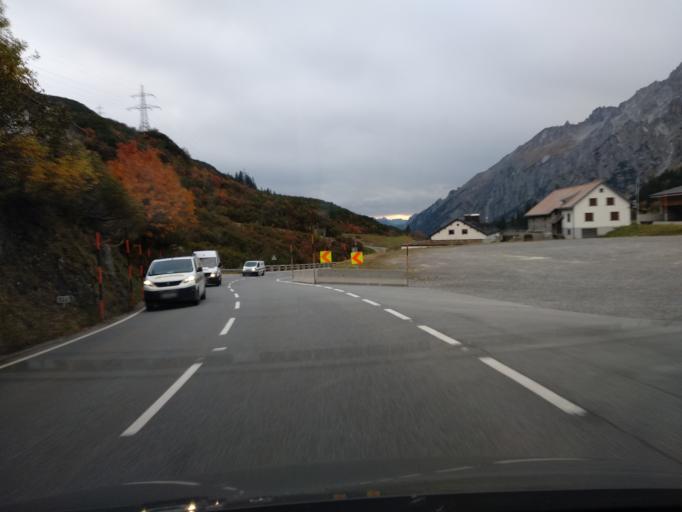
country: AT
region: Vorarlberg
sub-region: Politischer Bezirk Bludenz
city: Lech
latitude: 47.1375
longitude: 10.1801
